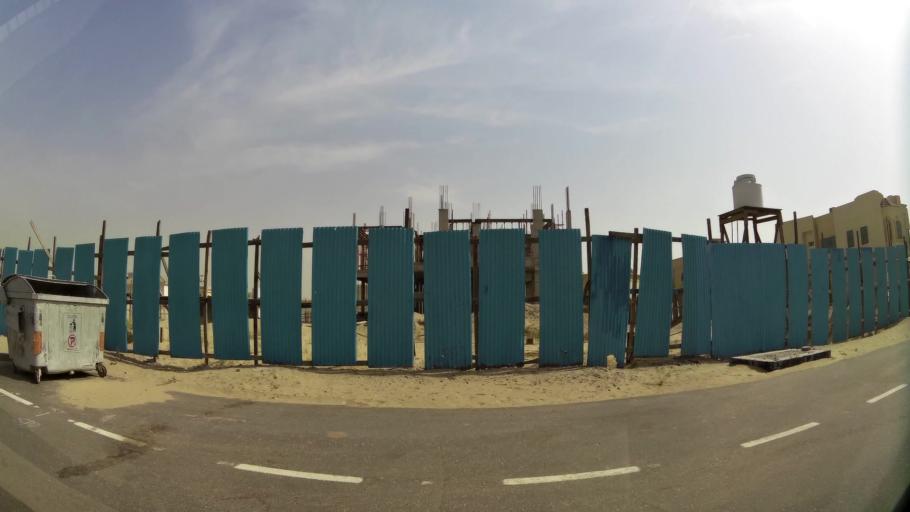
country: AE
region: Ash Shariqah
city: Sharjah
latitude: 25.2652
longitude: 55.4678
